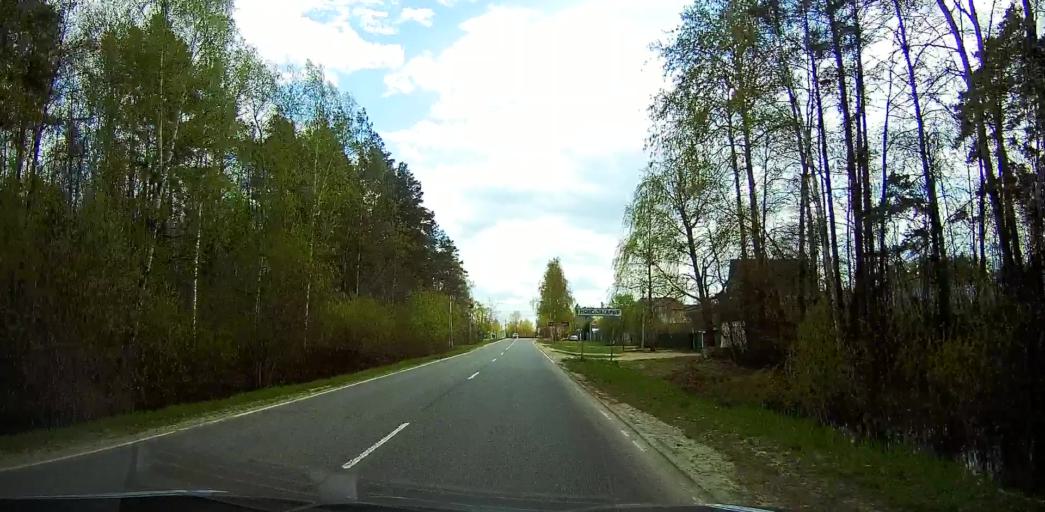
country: RU
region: Moskovskaya
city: Davydovo
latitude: 55.6502
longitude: 38.7550
